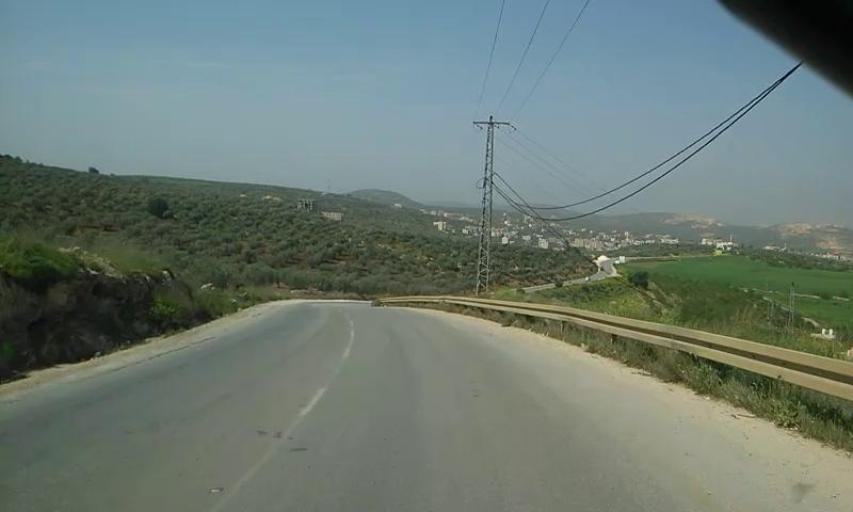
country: PS
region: West Bank
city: Az Zababidah
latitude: 32.3751
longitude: 35.3363
